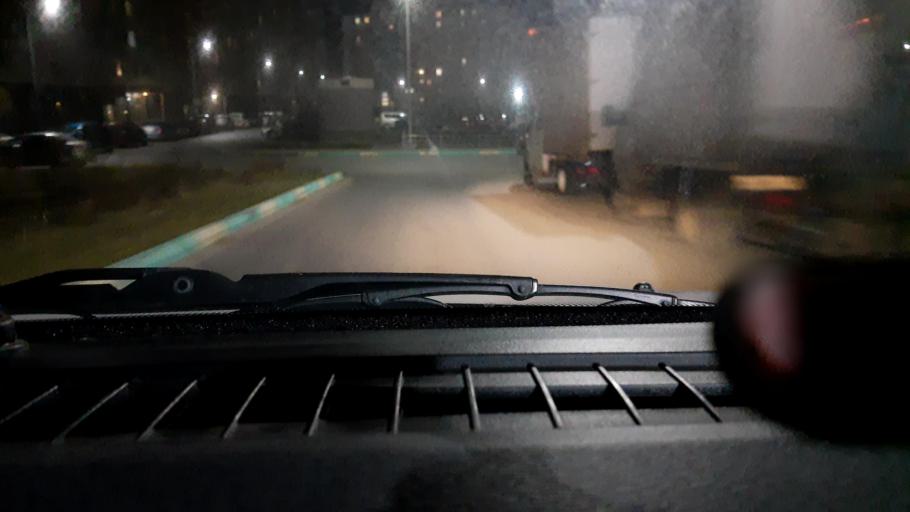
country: RU
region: Nizjnij Novgorod
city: Gorbatovka
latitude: 56.3607
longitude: 43.7972
